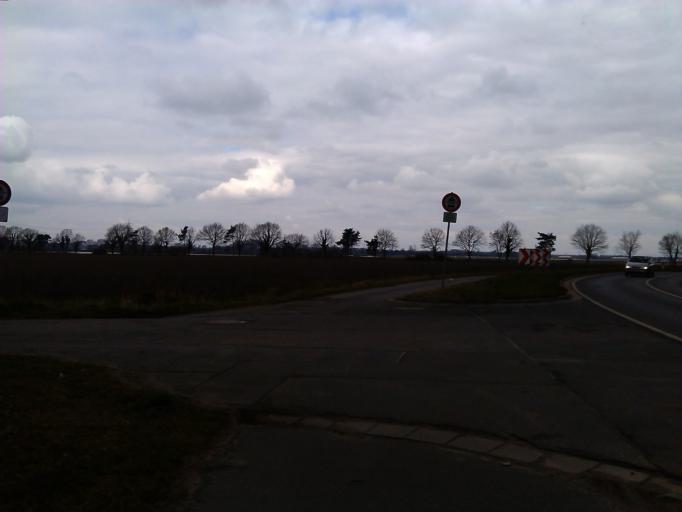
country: DE
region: Hesse
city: Griesheim
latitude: 49.8299
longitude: 8.5638
